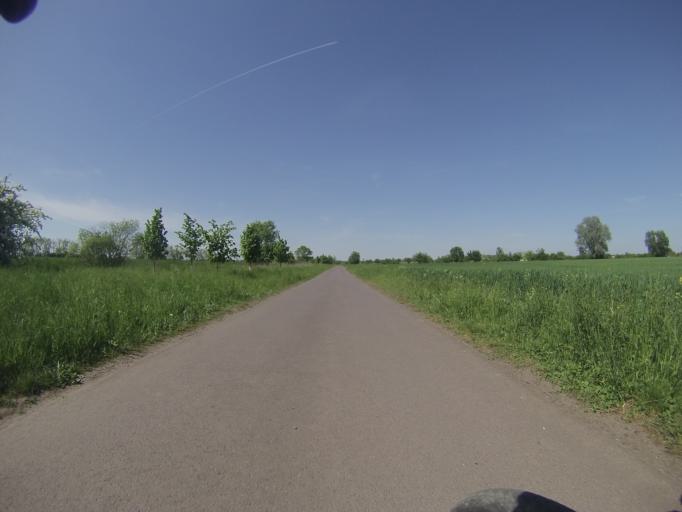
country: CZ
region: South Moravian
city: Novosedly
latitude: 48.8050
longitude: 16.4871
